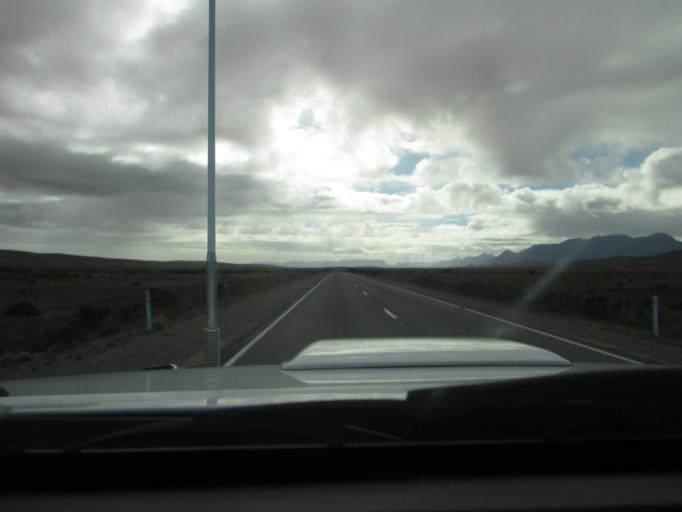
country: AU
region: South Australia
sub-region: Flinders Ranges
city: Quorn
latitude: -31.6137
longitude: 138.3966
